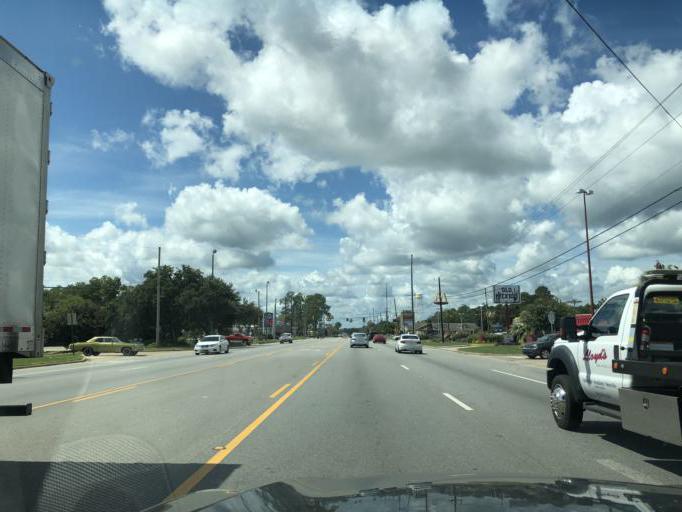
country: US
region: Alabama
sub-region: Barbour County
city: Eufaula
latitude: 31.8779
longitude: -85.1495
